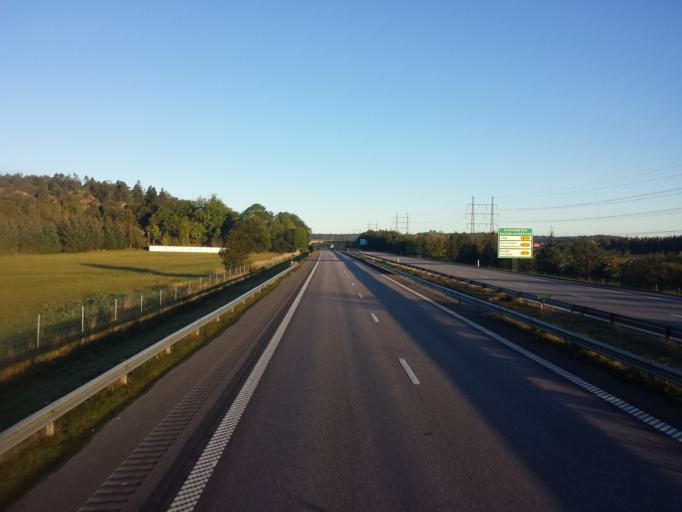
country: SE
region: Halland
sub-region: Kungsbacka Kommun
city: Kungsbacka
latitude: 57.4604
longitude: 12.0808
